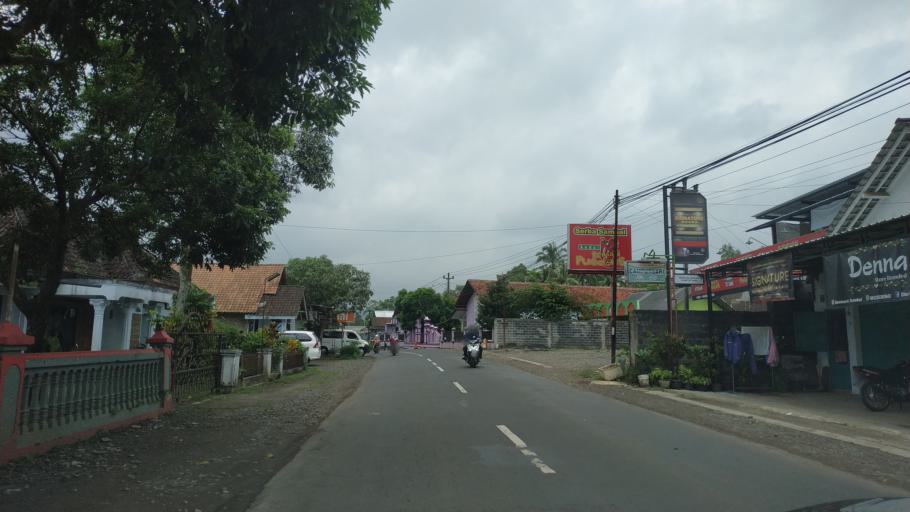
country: ID
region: Central Java
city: Weleri
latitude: -7.0813
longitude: 110.0428
